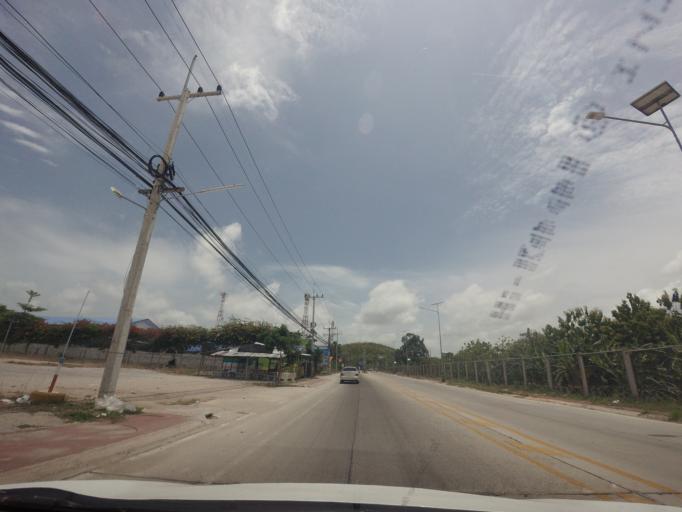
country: TH
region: Chon Buri
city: Sattahip
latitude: 12.6430
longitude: 100.9543
